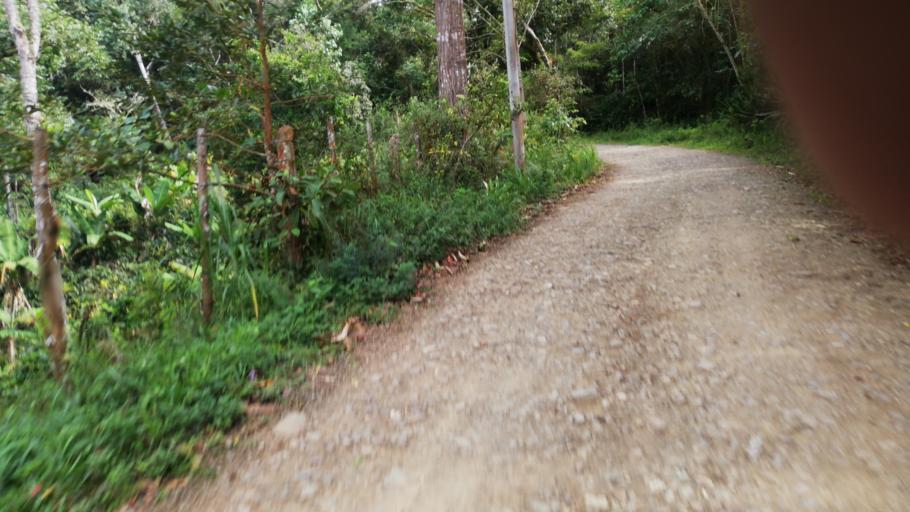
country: CO
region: Valle del Cauca
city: Yumbo
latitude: 3.6293
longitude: -76.5466
